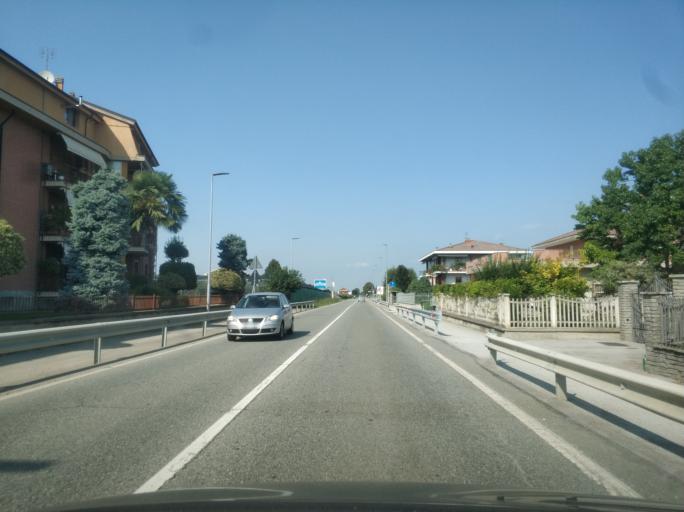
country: IT
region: Piedmont
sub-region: Provincia di Cuneo
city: Centallo
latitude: 44.5058
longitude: 7.5873
